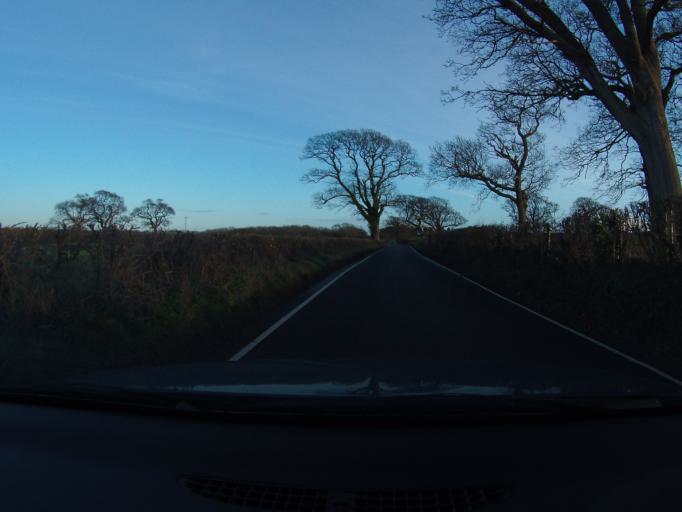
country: GB
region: England
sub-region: Isle of Wight
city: Brading
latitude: 50.6902
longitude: -1.1592
